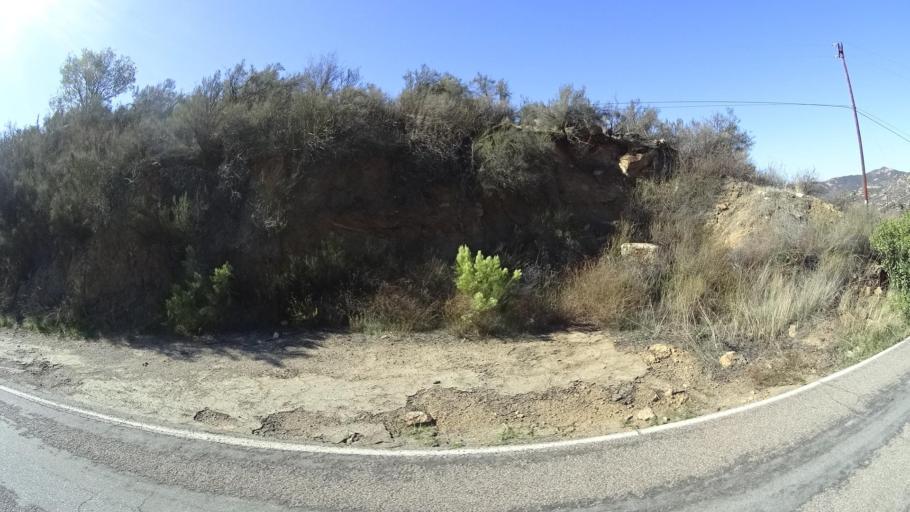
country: US
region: California
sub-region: San Diego County
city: Jamul
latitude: 32.7084
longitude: -116.7882
